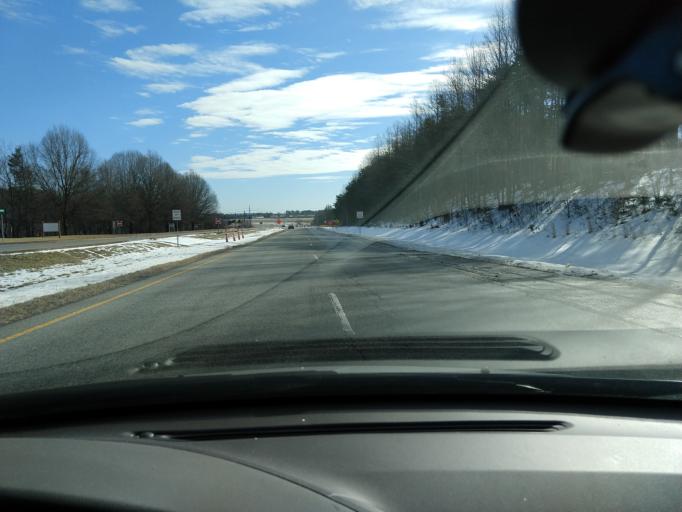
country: US
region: North Carolina
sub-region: Guilford County
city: Oak Ridge
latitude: 36.1079
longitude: -79.9589
